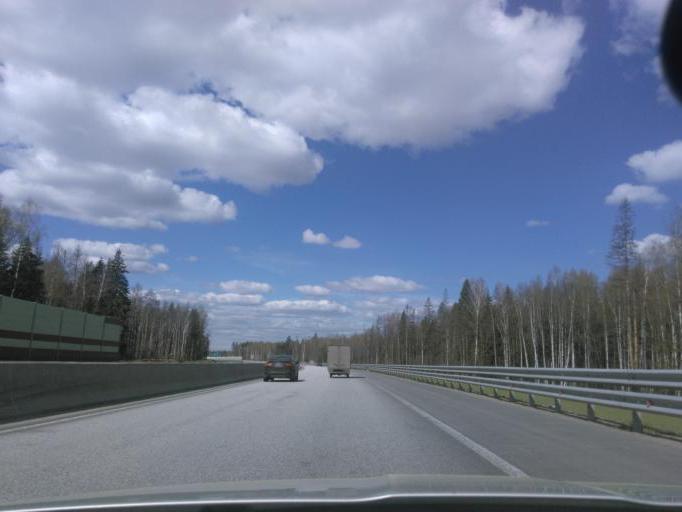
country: RU
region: Moskovskaya
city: Peshki
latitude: 56.1402
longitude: 37.0891
